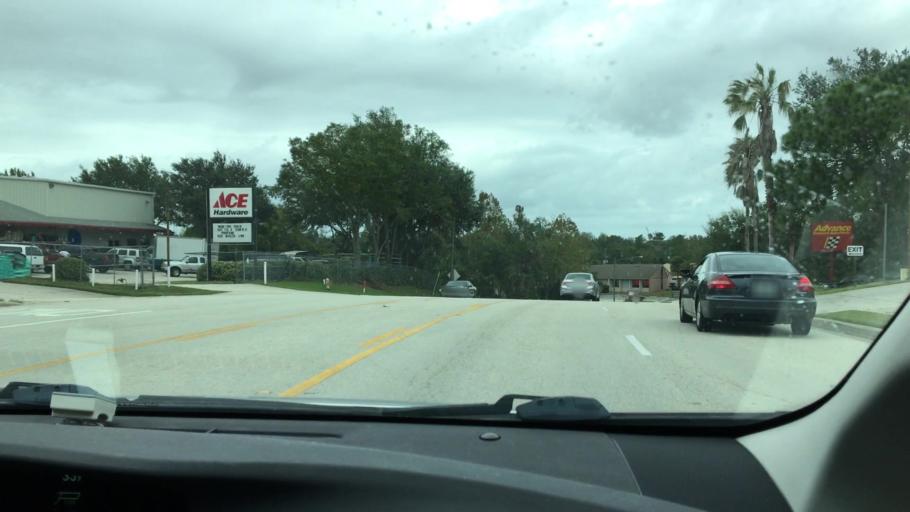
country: US
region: Florida
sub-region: Volusia County
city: Deltona
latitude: 28.9041
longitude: -81.2279
